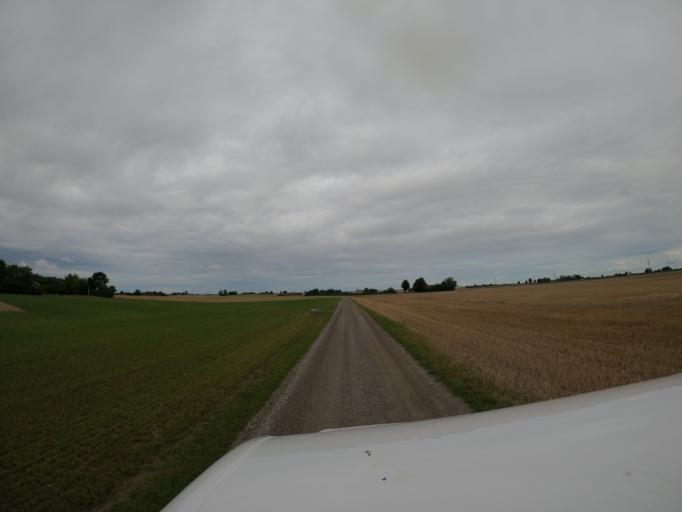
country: SE
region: Skane
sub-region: Kavlinge Kommun
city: Kaevlinge
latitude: 55.7513
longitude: 13.1287
